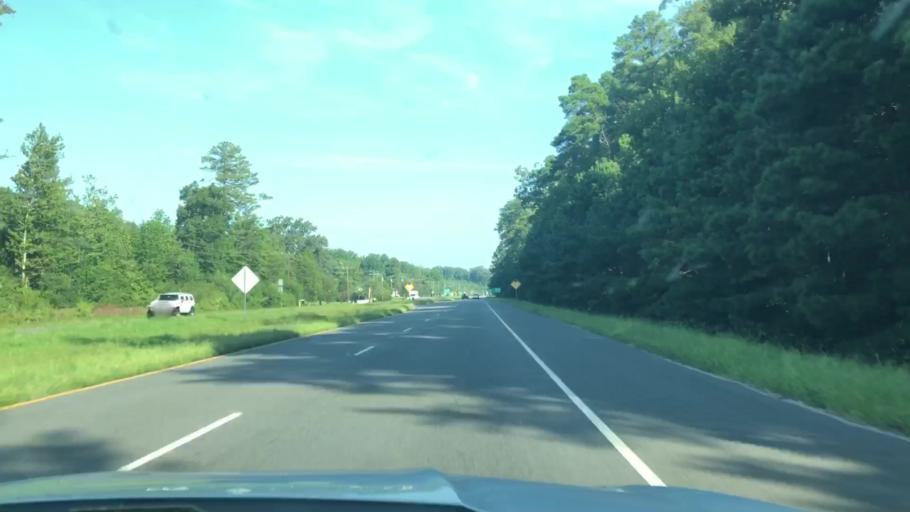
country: US
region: Virginia
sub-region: Essex County
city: Tappahannock
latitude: 37.8900
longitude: -76.8671
